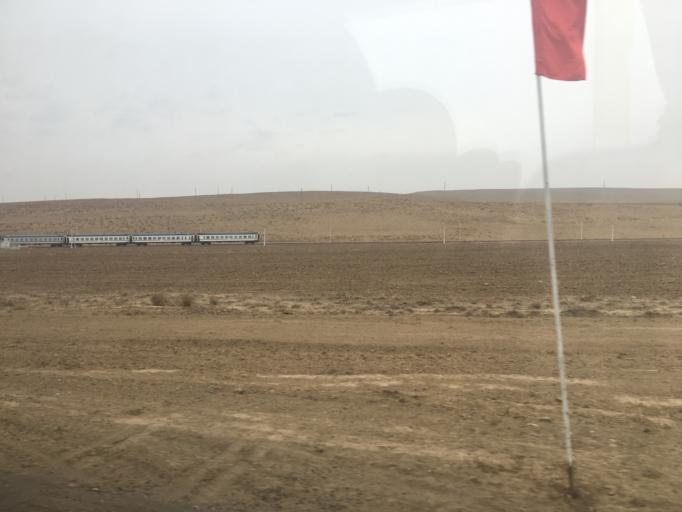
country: TM
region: Mary
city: Serhetabat
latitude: 35.4701
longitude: 62.4066
